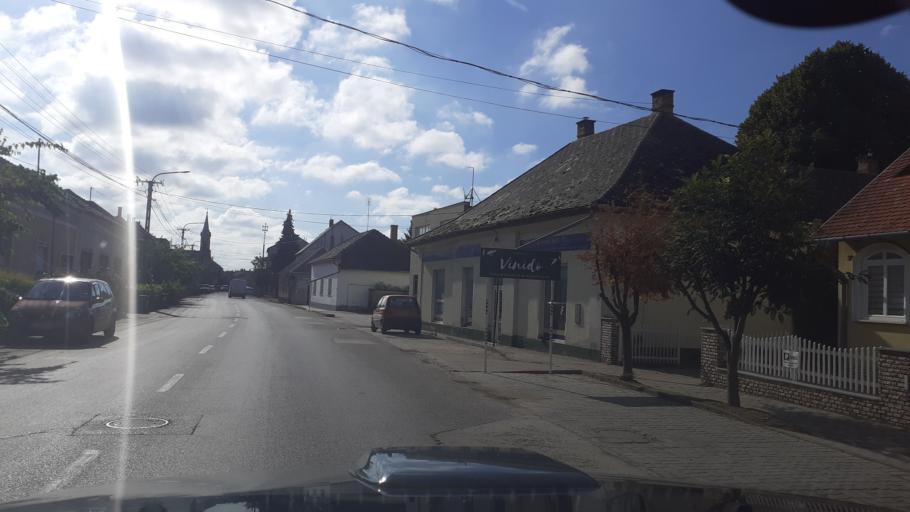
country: HU
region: Tolna
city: Dunafoldvar
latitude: 46.8106
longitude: 18.9214
